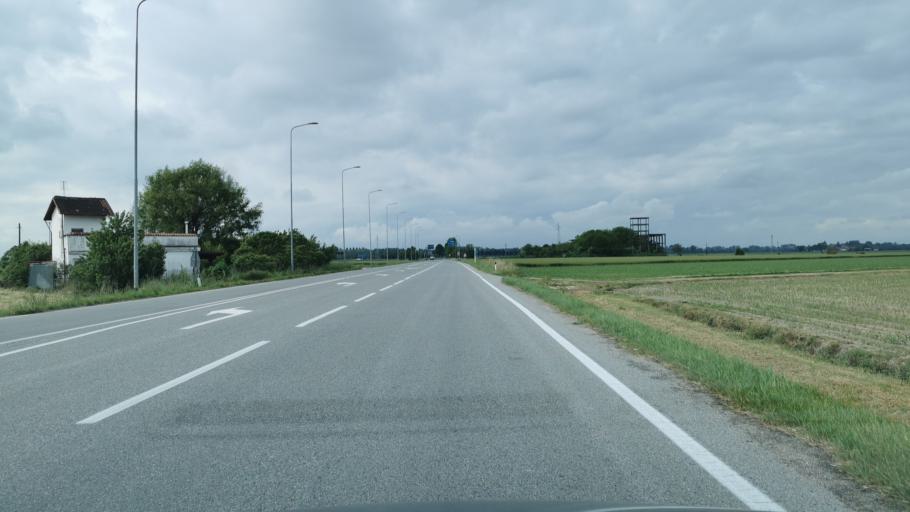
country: IT
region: Piedmont
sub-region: Provincia di Cuneo
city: Racconigi
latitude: 44.8059
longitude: 7.6945
